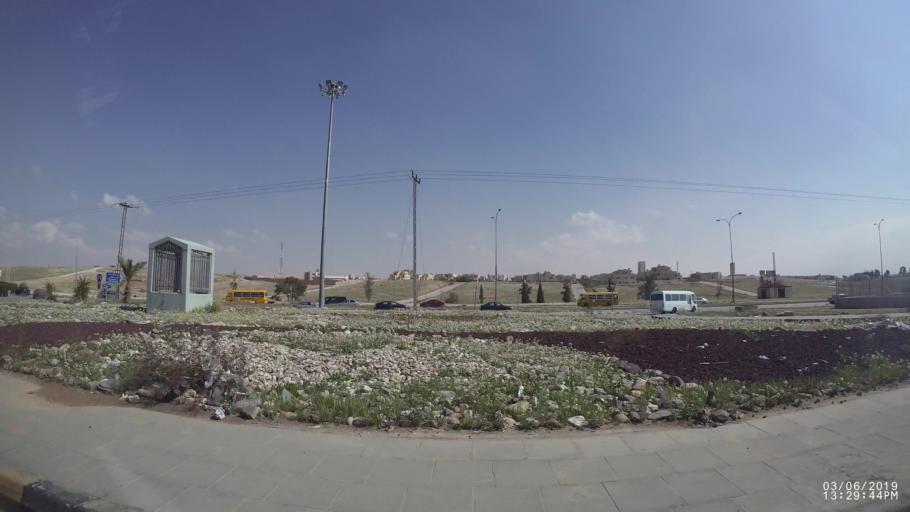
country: JO
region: Zarqa
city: Zarqa
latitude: 32.0805
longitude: 36.1066
